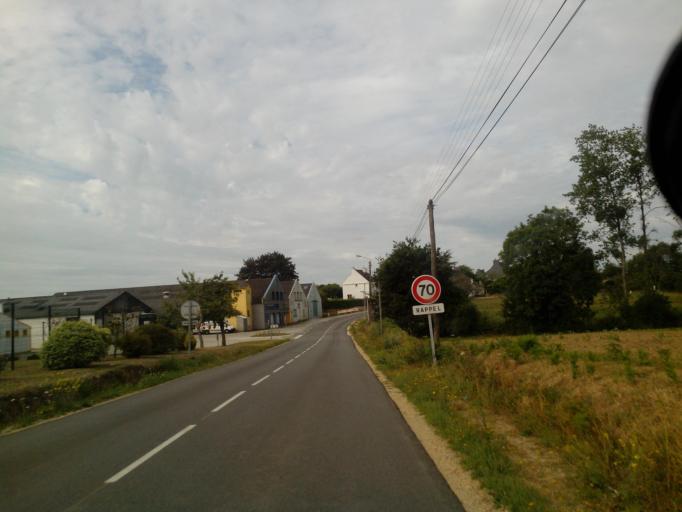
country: FR
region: Brittany
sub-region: Departement du Morbihan
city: Ploemel
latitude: 47.6557
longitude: -3.0588
